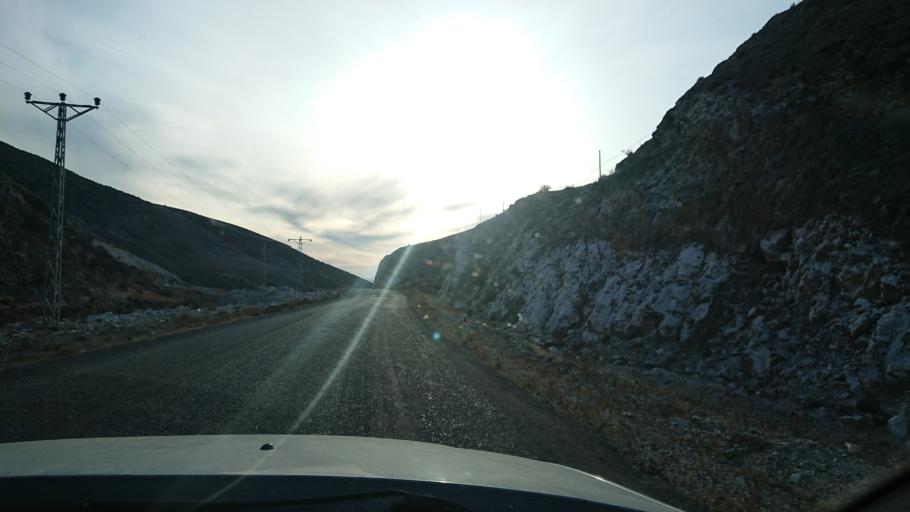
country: TR
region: Ankara
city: Sereflikochisar
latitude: 38.7516
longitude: 33.6909
